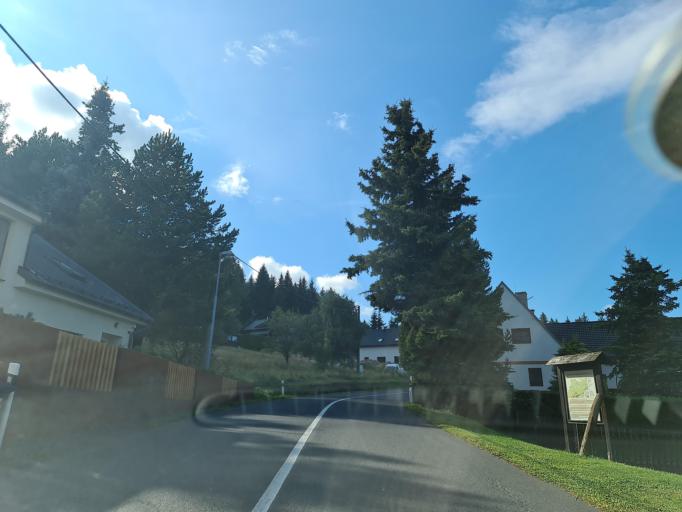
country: CZ
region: Ustecky
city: Mezibori
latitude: 50.6282
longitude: 13.5648
